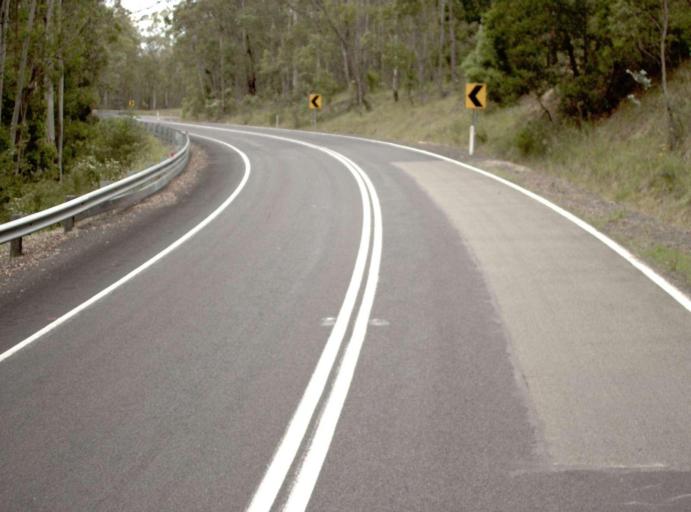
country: AU
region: New South Wales
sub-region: Bombala
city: Bombala
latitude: -37.2924
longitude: 149.2164
